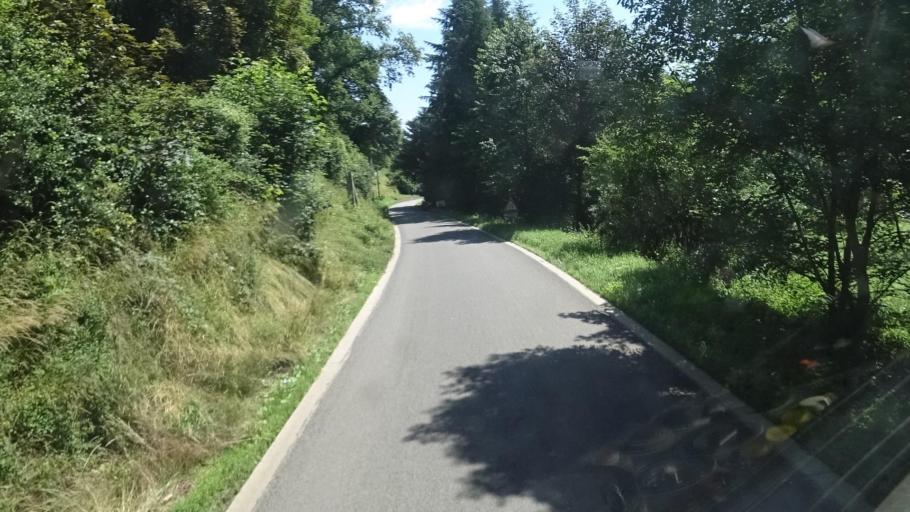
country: BE
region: Wallonia
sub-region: Province de Namur
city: Profondeville
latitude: 50.3491
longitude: 4.8458
